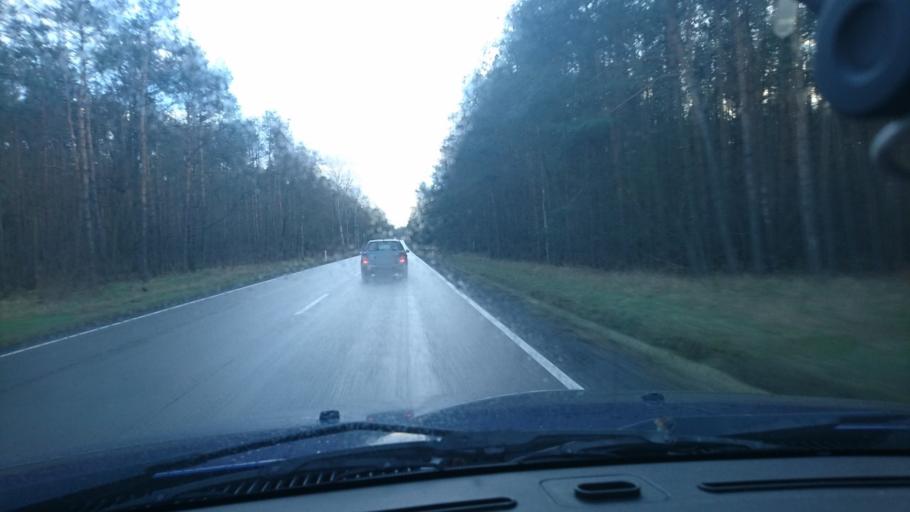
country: PL
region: Greater Poland Voivodeship
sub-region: Powiat kepinski
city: Bralin
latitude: 51.3460
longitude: 17.9508
